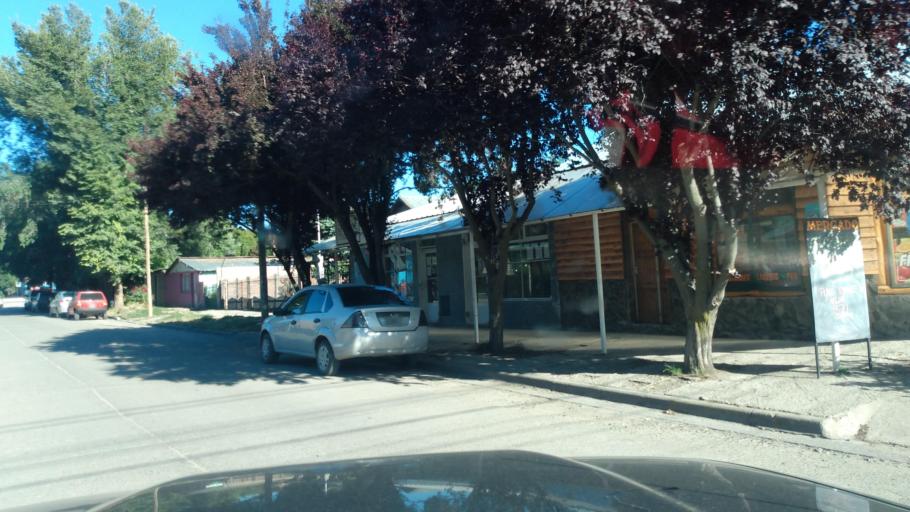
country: AR
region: Neuquen
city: Junin de los Andes
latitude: -39.9485
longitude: -71.0738
